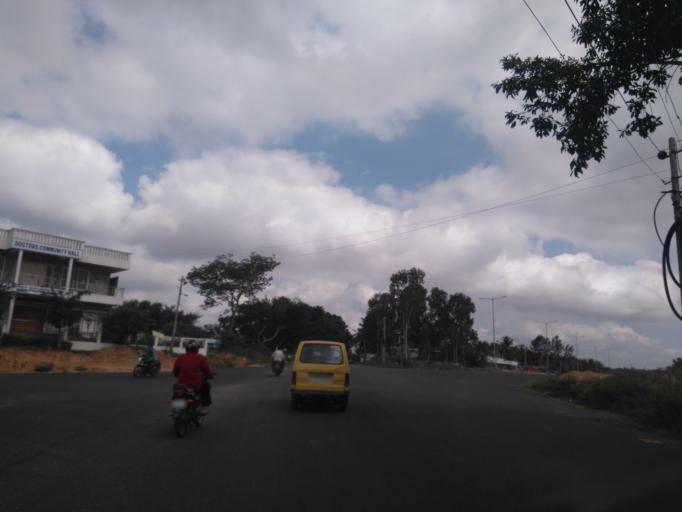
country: IN
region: Karnataka
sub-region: Mysore
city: Mysore
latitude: 12.2930
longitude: 76.7059
